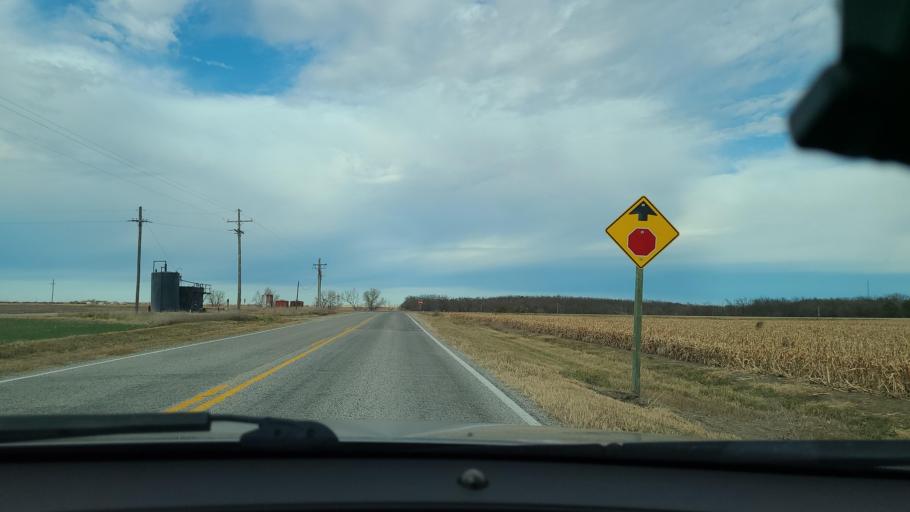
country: US
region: Kansas
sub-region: McPherson County
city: Inman
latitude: 38.3755
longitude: -97.9244
